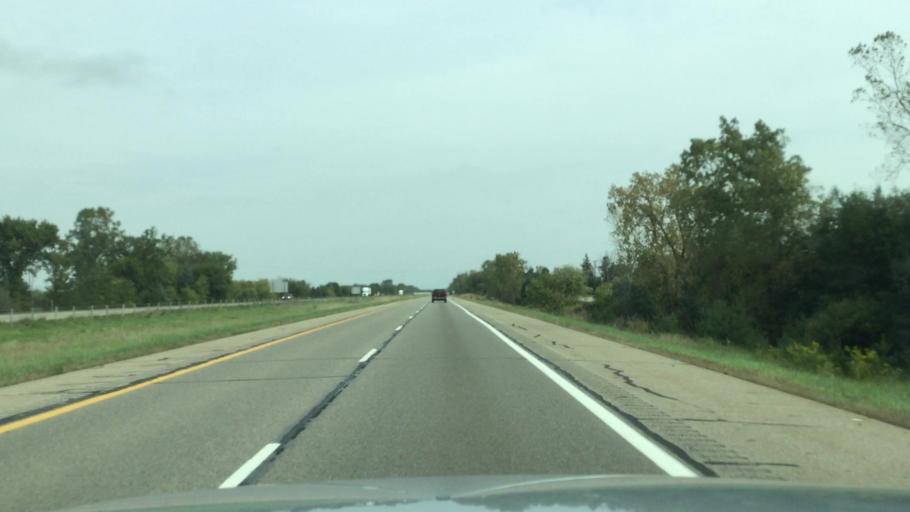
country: US
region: Michigan
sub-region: Shiawassee County
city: Durand
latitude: 42.9375
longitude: -83.9859
